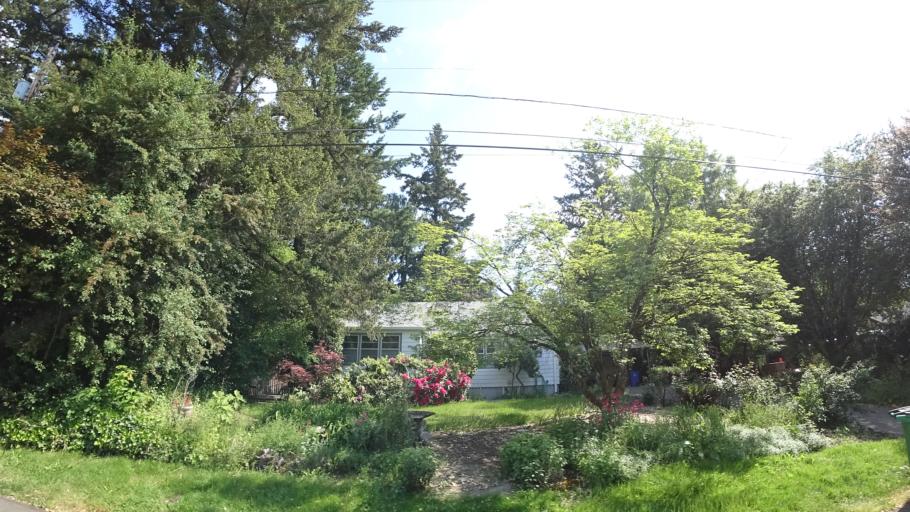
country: US
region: Oregon
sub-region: Washington County
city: Garden Home-Whitford
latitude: 45.4561
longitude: -122.7425
